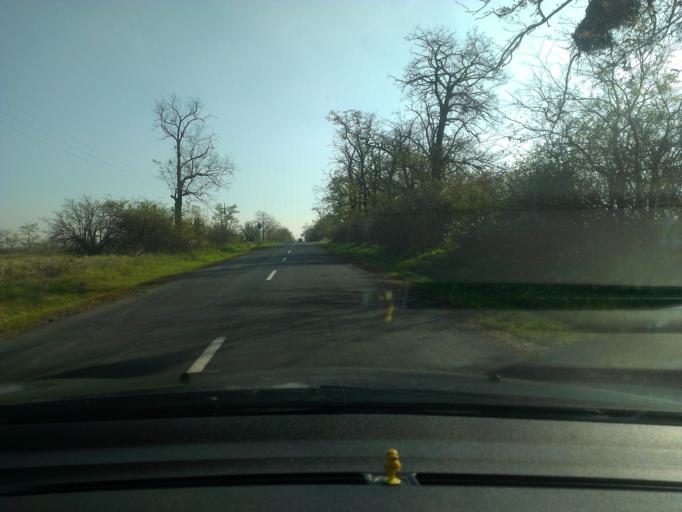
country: HU
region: Komarom-Esztergom
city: Mocsa
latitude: 47.7012
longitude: 18.2133
